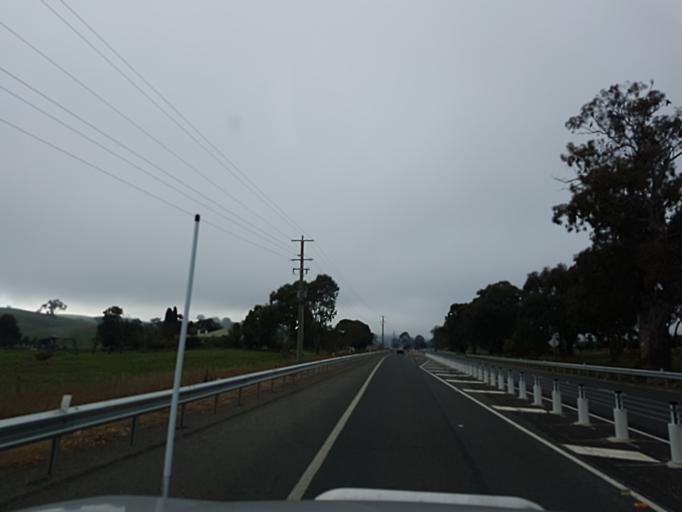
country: AU
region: Victoria
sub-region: Murrindindi
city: Alexandra
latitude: -37.2050
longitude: 145.4611
